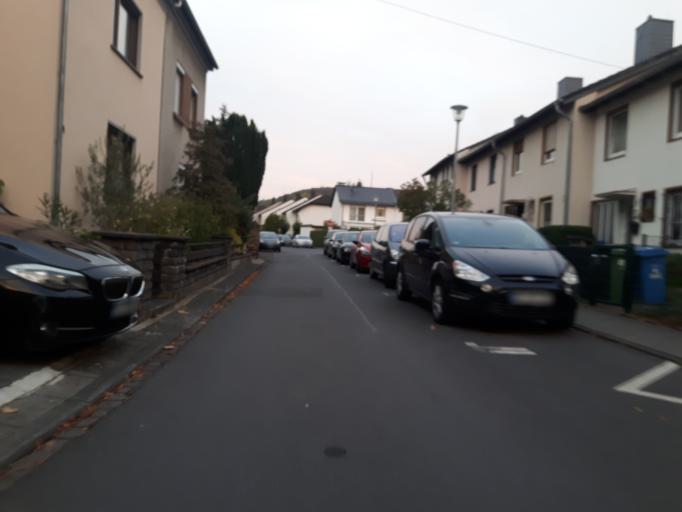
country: DE
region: Rheinland-Pfalz
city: Unkel
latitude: 50.5970
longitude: 7.2134
